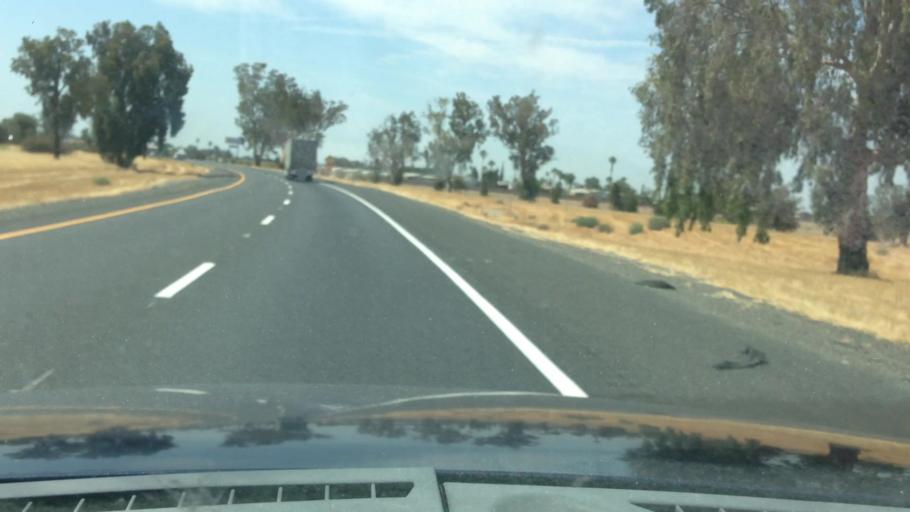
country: US
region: California
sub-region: Tulare County
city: Tulare
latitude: 36.1601
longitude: -119.3333
